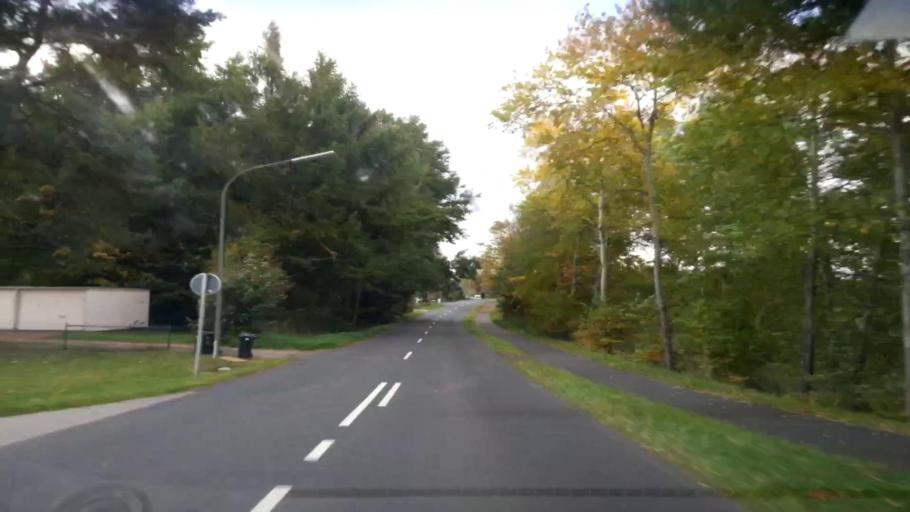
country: DE
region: Bavaria
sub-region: Upper Palatinate
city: Waldsassen
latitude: 50.0205
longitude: 12.3223
